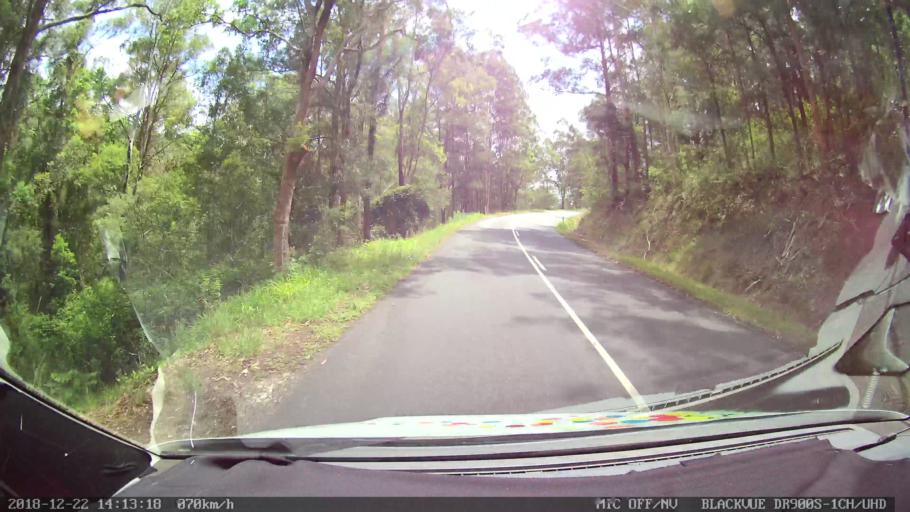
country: AU
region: New South Wales
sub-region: Clarence Valley
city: Coutts Crossing
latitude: -29.9994
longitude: 152.6995
